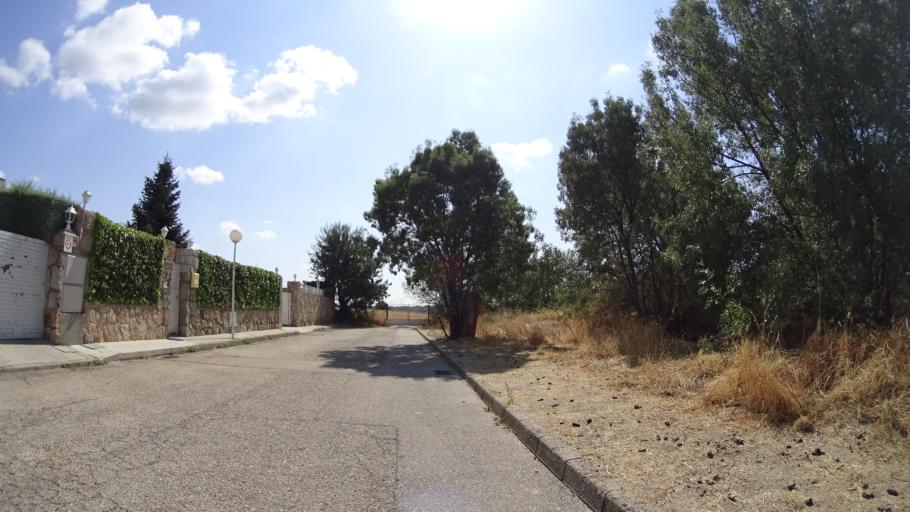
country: ES
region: Madrid
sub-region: Provincia de Madrid
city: Galapagar
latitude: 40.5817
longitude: -3.9905
